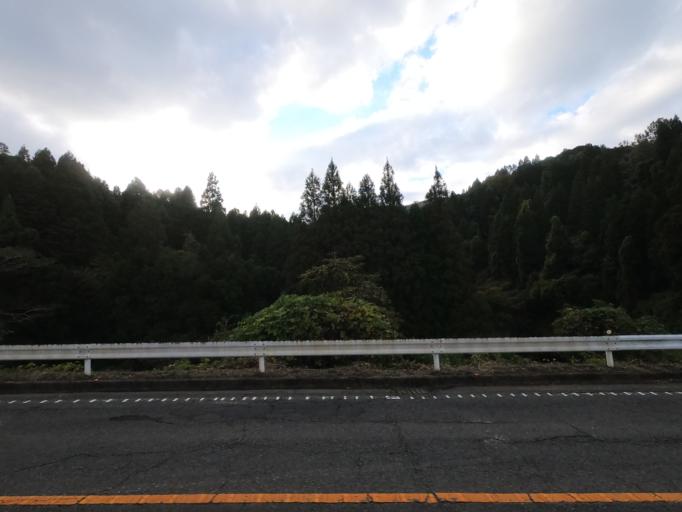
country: JP
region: Kumamoto
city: Minamata
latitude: 32.2508
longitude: 130.5027
